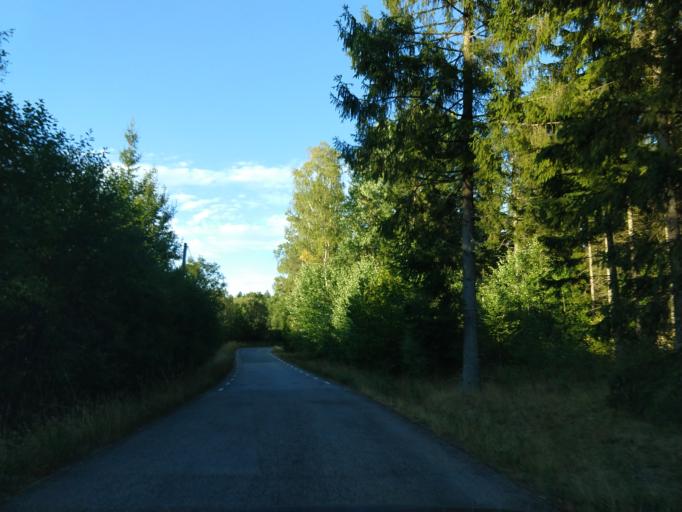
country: SE
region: Blekinge
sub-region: Ronneby Kommun
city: Brakne-Hoby
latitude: 56.2670
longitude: 15.1495
